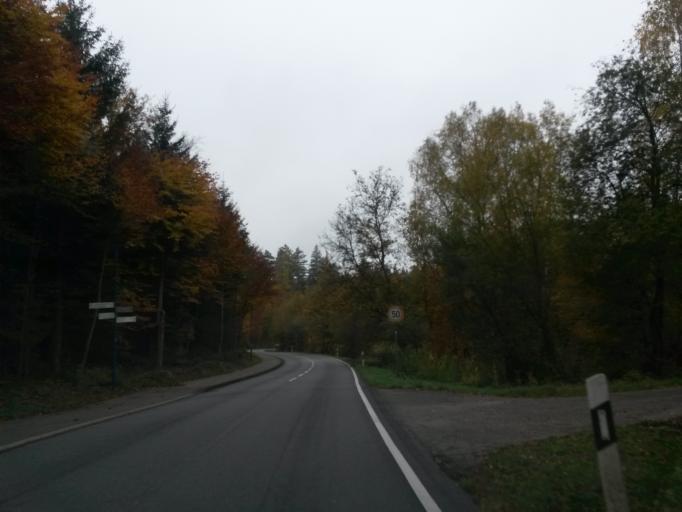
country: DE
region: Baden-Wuerttemberg
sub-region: Karlsruhe Region
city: Ettlingen
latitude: 48.9160
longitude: 8.4756
